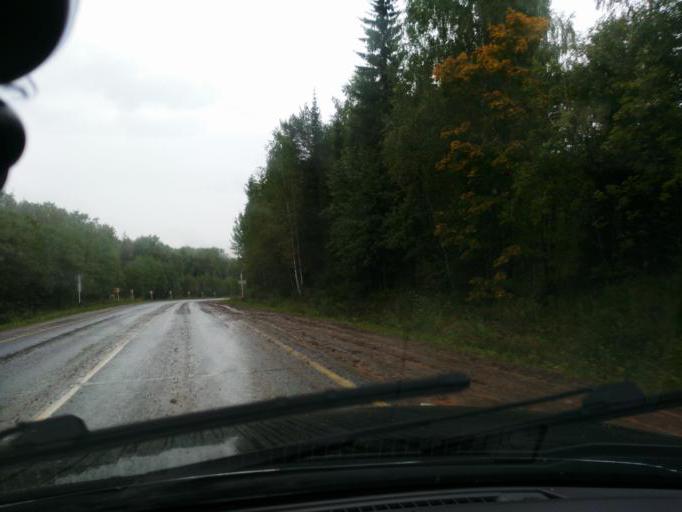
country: RU
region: Perm
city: Yugo-Kamskiy
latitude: 57.5175
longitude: 55.6865
